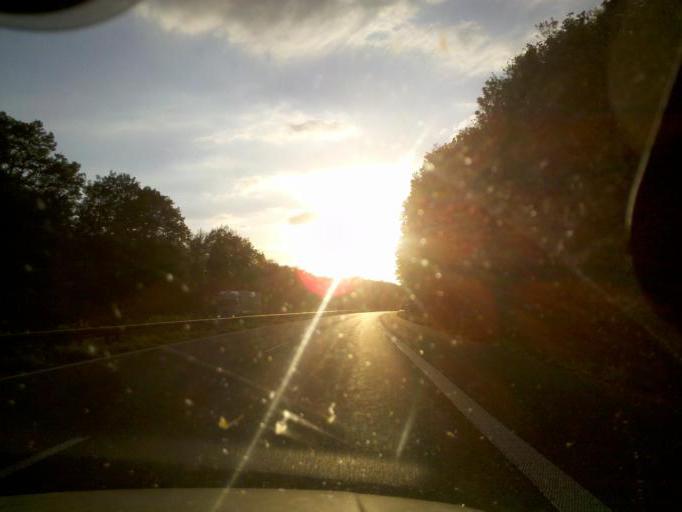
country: DE
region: North Rhine-Westphalia
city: Bergneustadt
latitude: 50.9661
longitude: 7.6596
